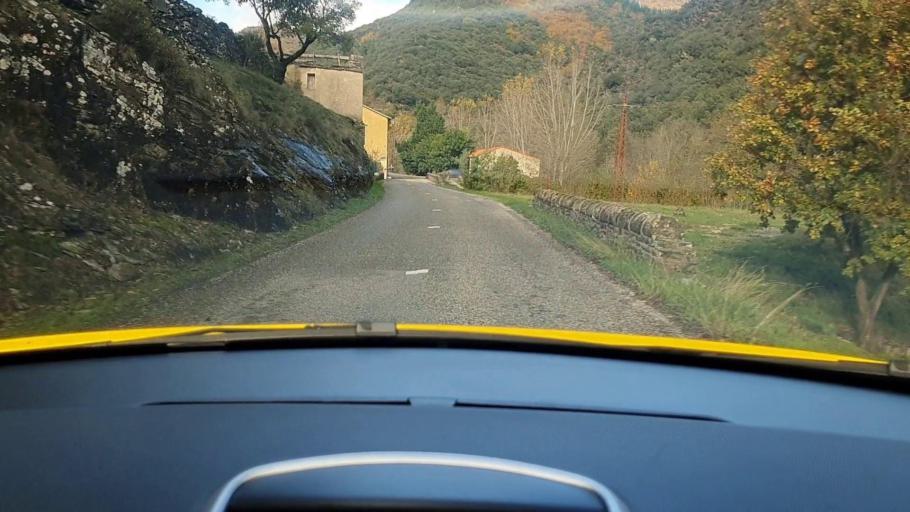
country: FR
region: Languedoc-Roussillon
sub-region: Departement du Gard
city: Valleraugue
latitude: 44.1670
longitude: 3.6599
